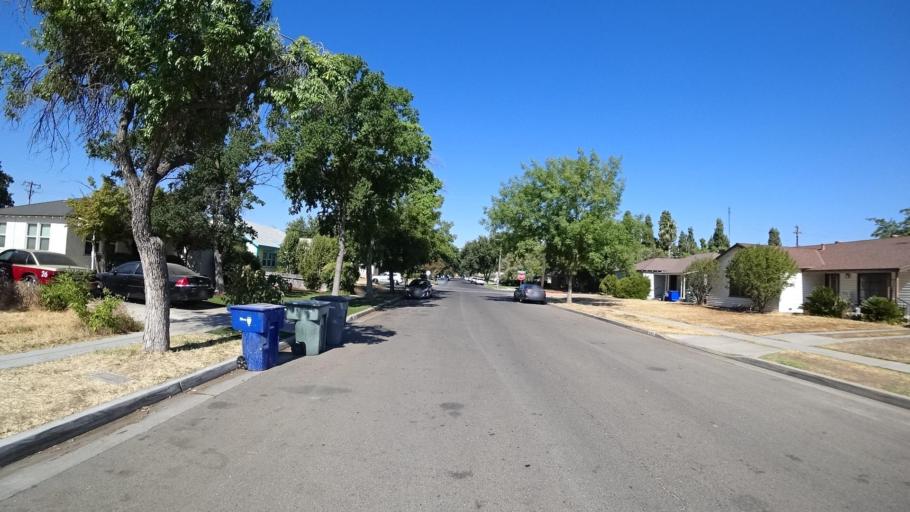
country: US
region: California
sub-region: Fresno County
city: Fresno
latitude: 36.7768
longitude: -119.7788
